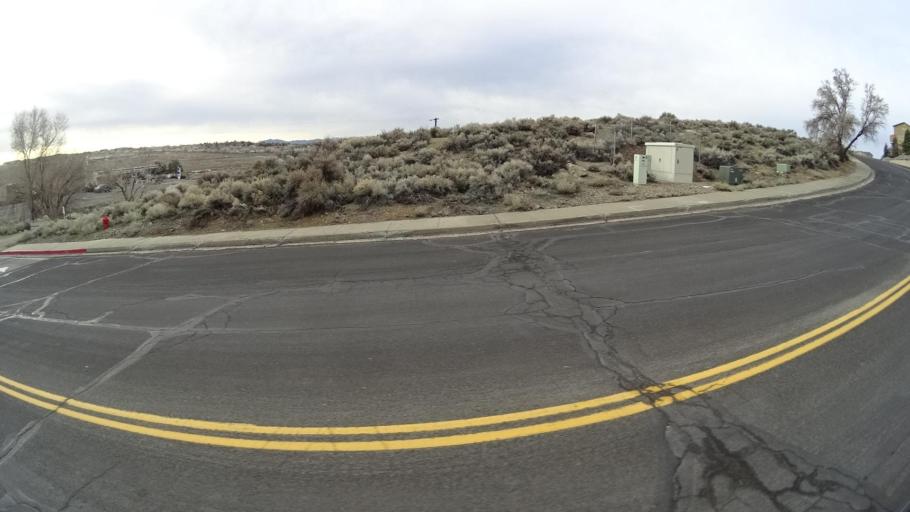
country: US
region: Nevada
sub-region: Washoe County
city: Reno
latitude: 39.5695
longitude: -119.8256
